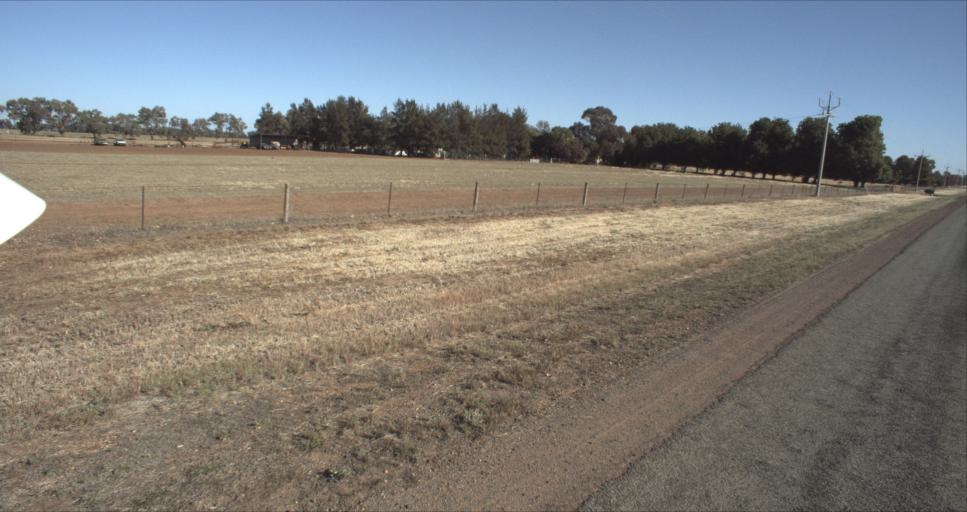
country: AU
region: New South Wales
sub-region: Leeton
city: Leeton
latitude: -34.5879
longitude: 146.2603
